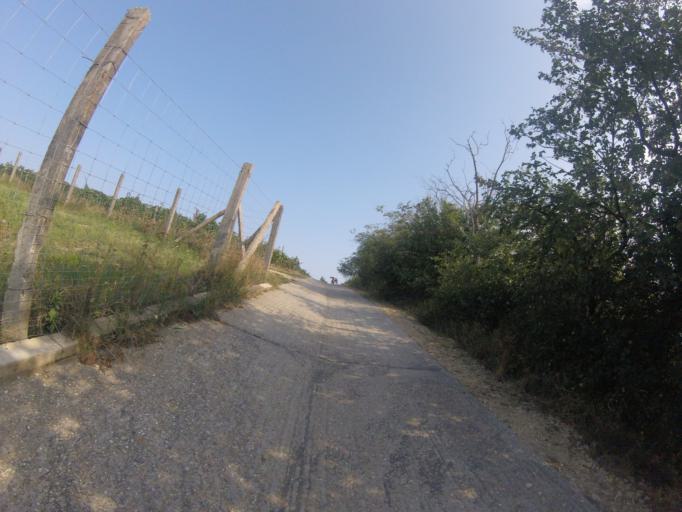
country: HU
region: Gyor-Moson-Sopron
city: Fertorakos
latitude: 47.6691
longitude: 16.6676
